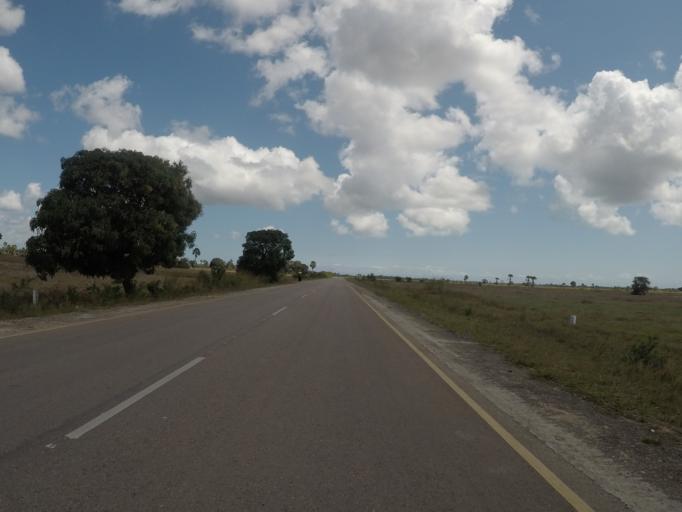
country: TZ
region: Zanzibar Central/South
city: Koani
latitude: -6.2001
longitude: 39.3693
